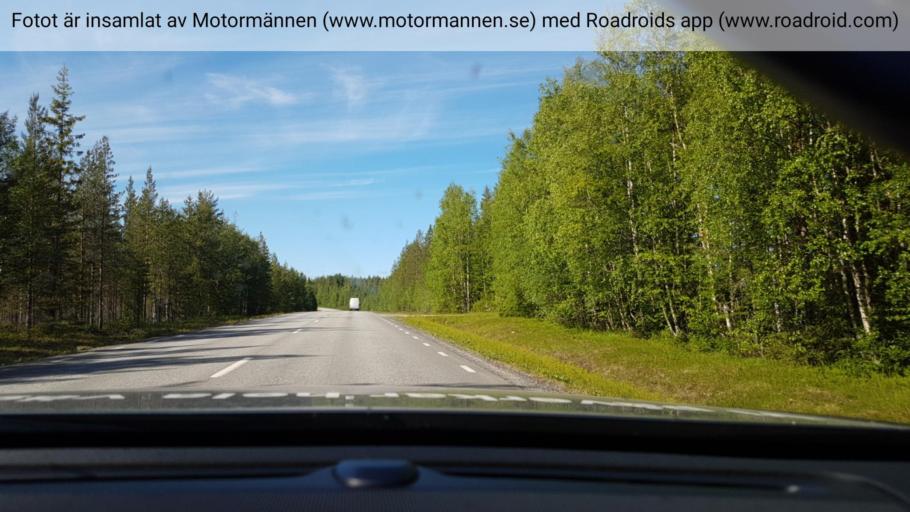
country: SE
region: Vaesterbotten
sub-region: Lycksele Kommun
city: Lycksele
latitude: 64.7103
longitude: 18.6958
